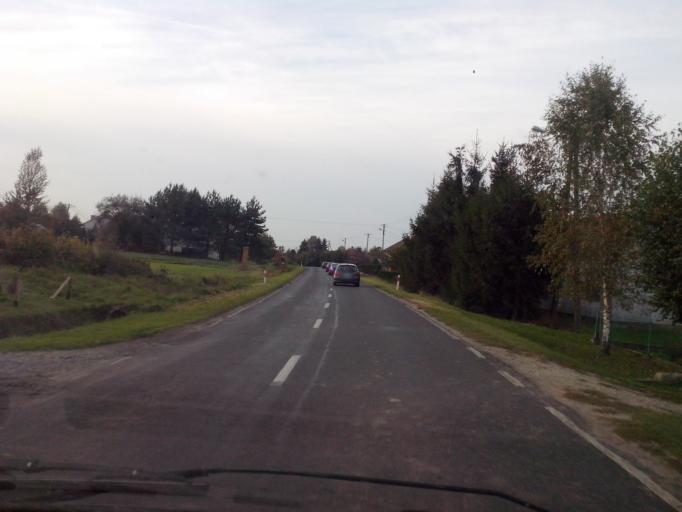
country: PL
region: Subcarpathian Voivodeship
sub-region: Powiat strzyzowski
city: Strzyzow
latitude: 49.8375
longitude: 21.8237
